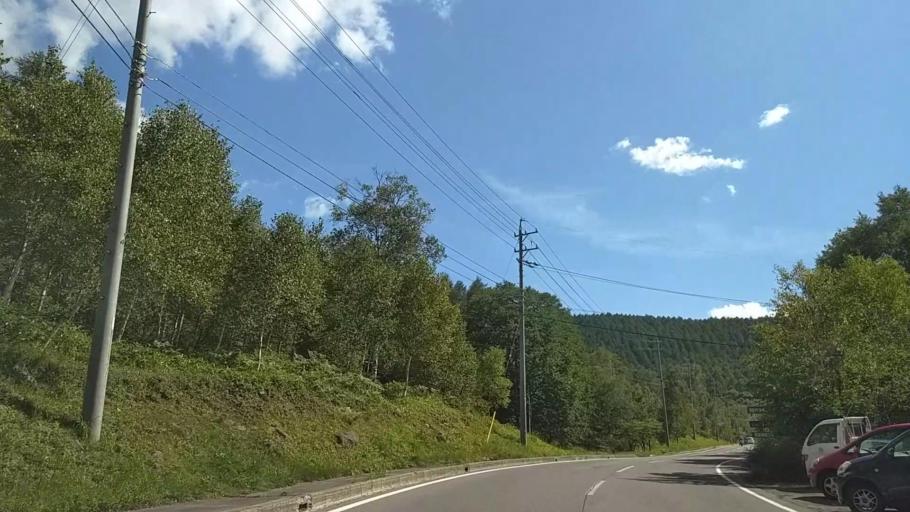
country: JP
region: Nagano
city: Chino
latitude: 36.1141
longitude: 138.2612
